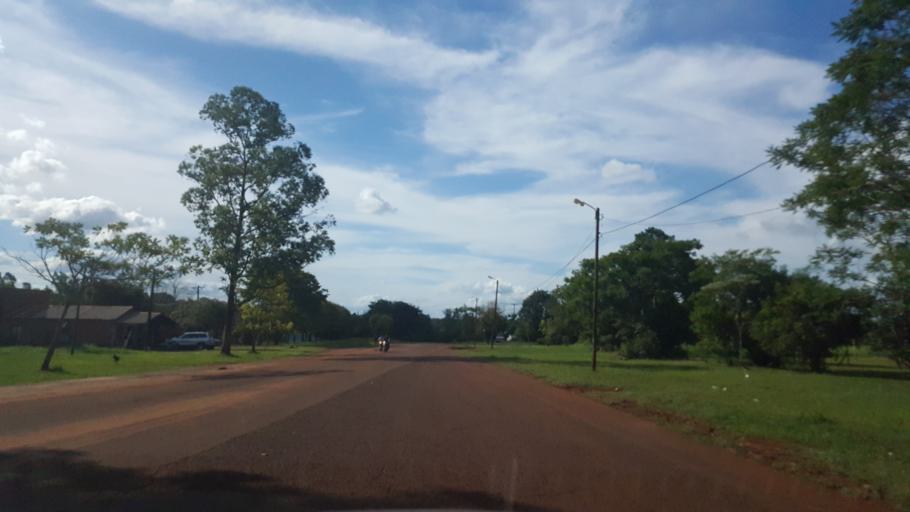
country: AR
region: Misiones
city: Santa Ana
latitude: -27.3670
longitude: -55.5833
